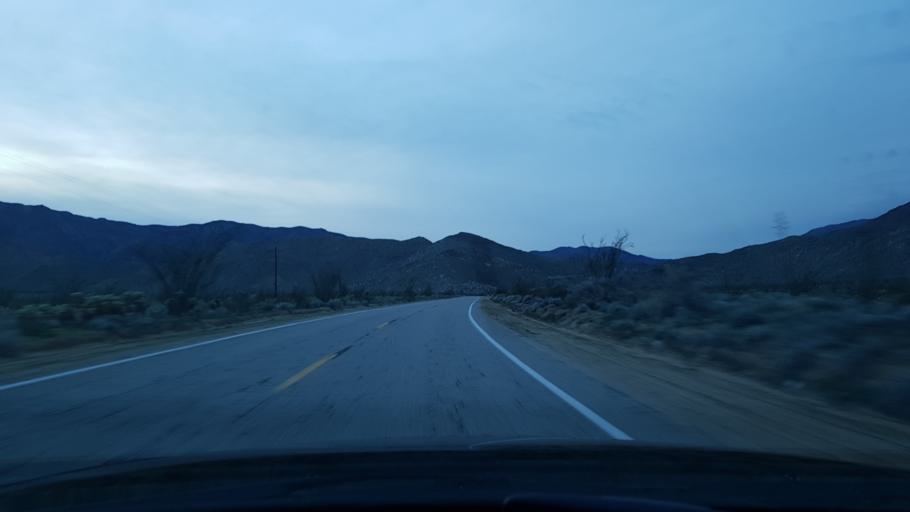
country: US
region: California
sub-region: San Diego County
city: Pine Valley
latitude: 32.9712
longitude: -116.3995
